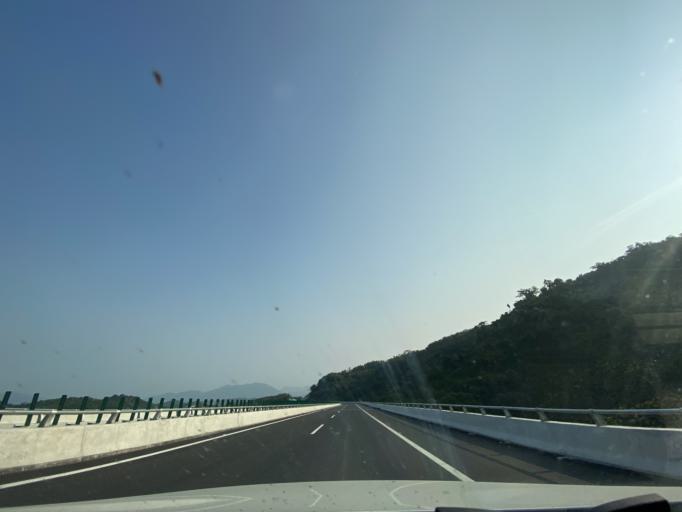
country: CN
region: Hainan
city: Xiangshui
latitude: 18.6569
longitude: 109.6289
